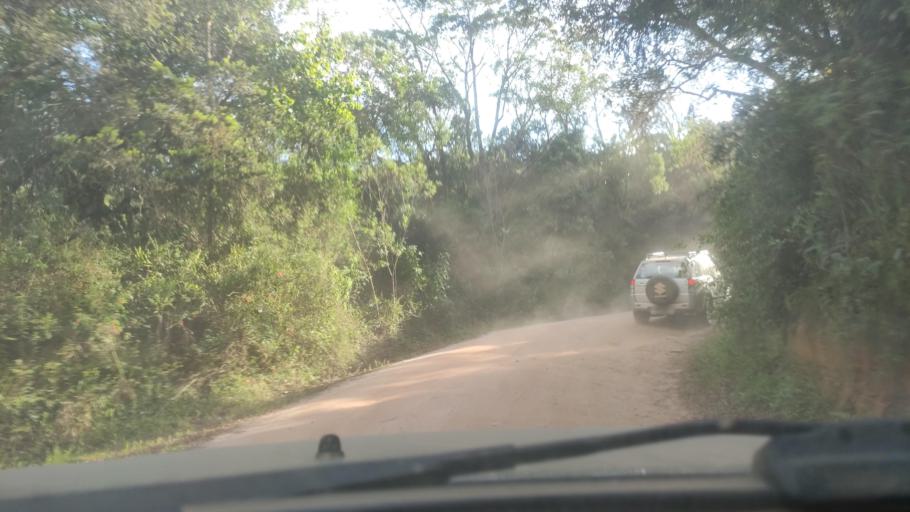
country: BR
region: Minas Gerais
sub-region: Camanducaia
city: Camanducaia
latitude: -22.7684
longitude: -45.9685
